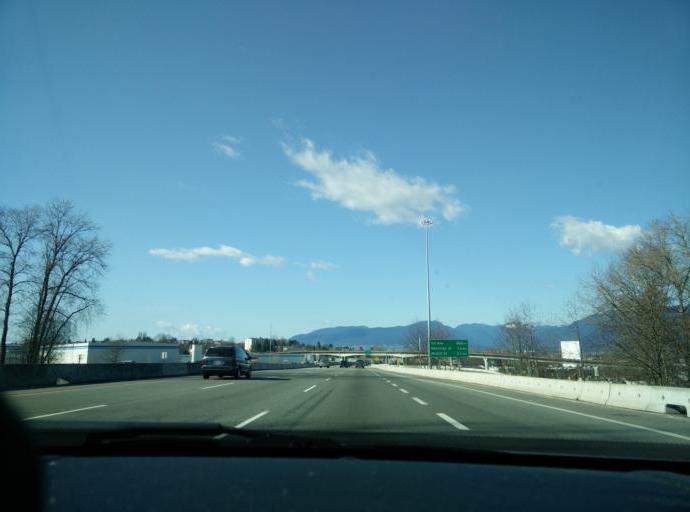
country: CA
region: British Columbia
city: Burnaby
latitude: 49.2597
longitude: -123.0214
